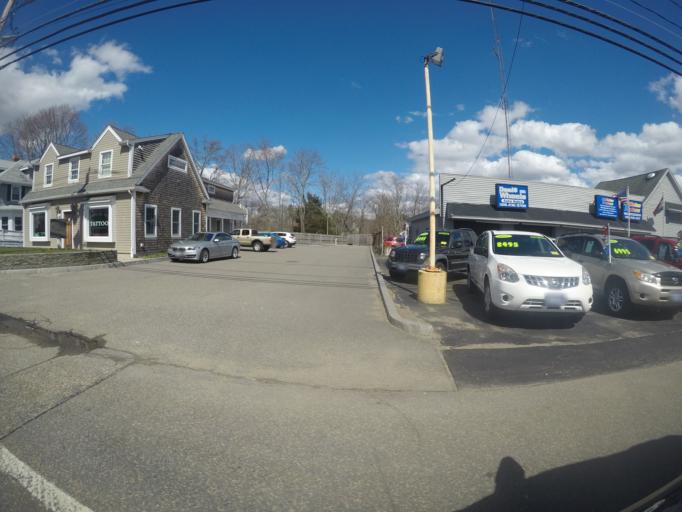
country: US
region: Massachusetts
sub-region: Bristol County
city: Easton
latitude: 42.0414
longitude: -71.0770
